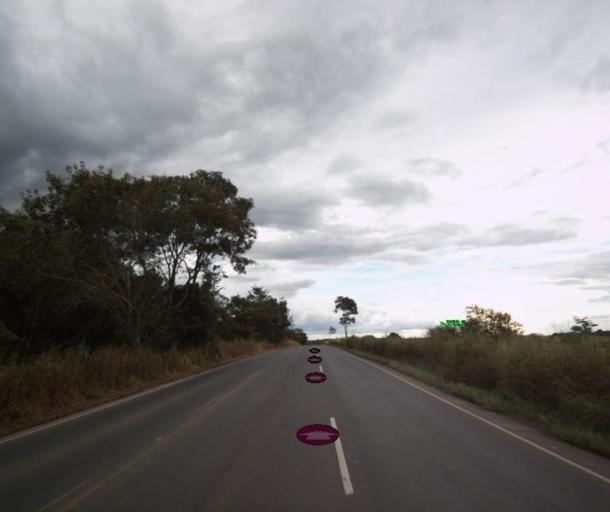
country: BR
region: Goias
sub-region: Itapaci
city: Itapaci
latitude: -14.9917
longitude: -49.4053
